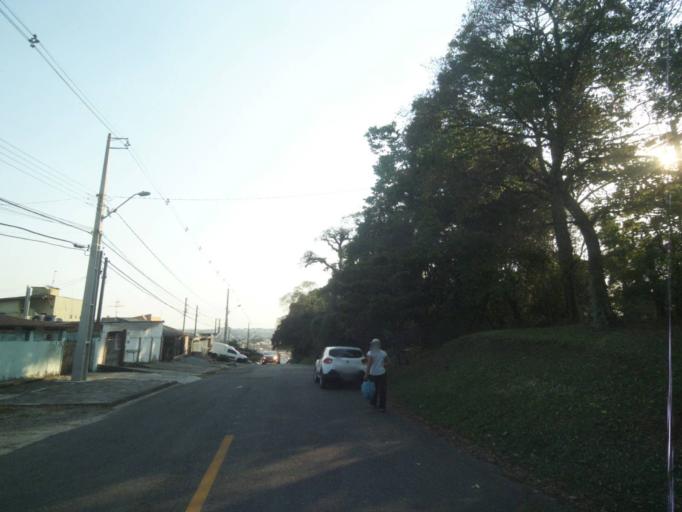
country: BR
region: Parana
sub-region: Sao Jose Dos Pinhais
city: Sao Jose dos Pinhais
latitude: -25.5283
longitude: -49.2539
